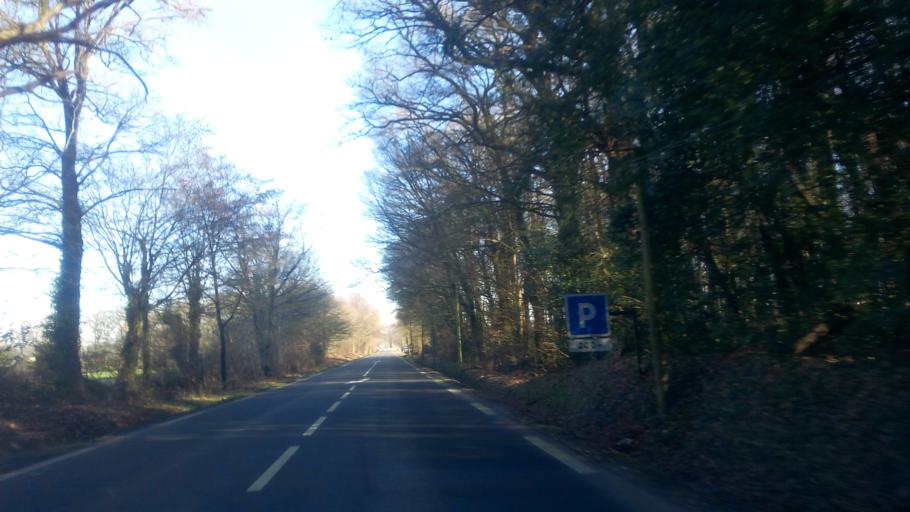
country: FR
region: Brittany
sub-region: Departement d'Ille-et-Vilaine
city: Sixt-sur-Aff
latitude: 47.7828
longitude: -2.0536
